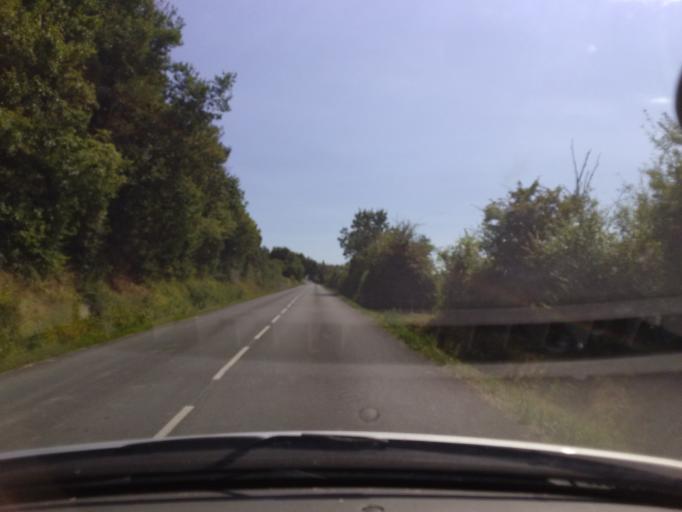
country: FR
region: Pays de la Loire
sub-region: Departement de la Vendee
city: Les Magnils-Reigniers
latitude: 46.4584
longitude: -1.2602
